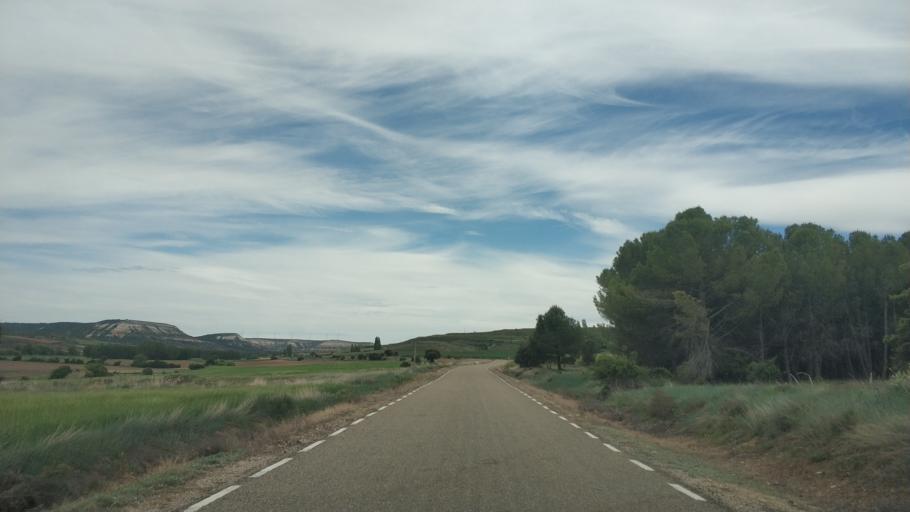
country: ES
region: Castille and Leon
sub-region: Provincia de Soria
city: Berlanga de Duero
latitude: 41.4389
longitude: -2.8166
